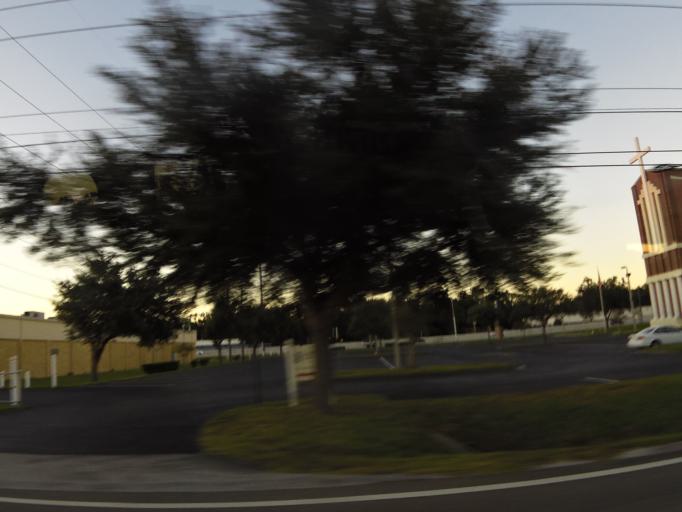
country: US
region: Florida
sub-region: Duval County
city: Jacksonville
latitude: 30.3141
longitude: -81.7476
